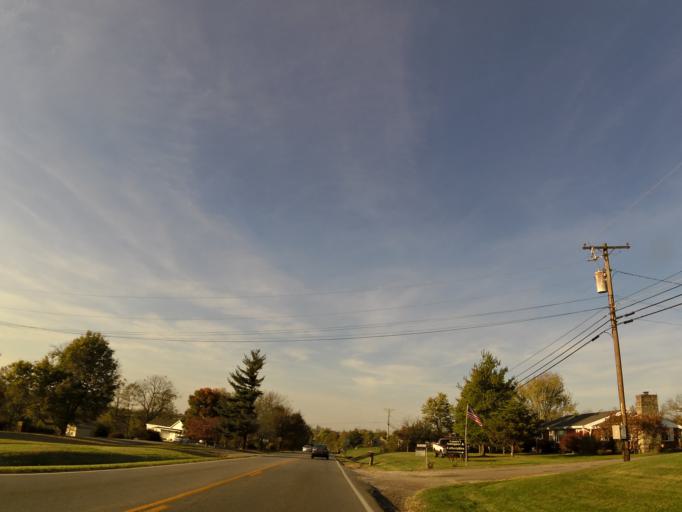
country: US
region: Kentucky
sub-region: Garrard County
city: Lancaster
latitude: 37.6313
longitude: -84.5808
